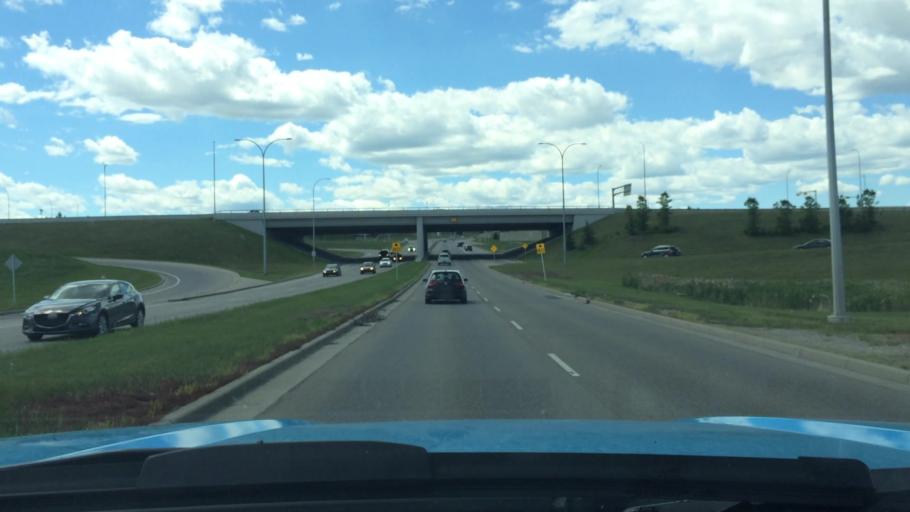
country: CA
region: Alberta
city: Calgary
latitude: 51.1445
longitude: -114.0899
